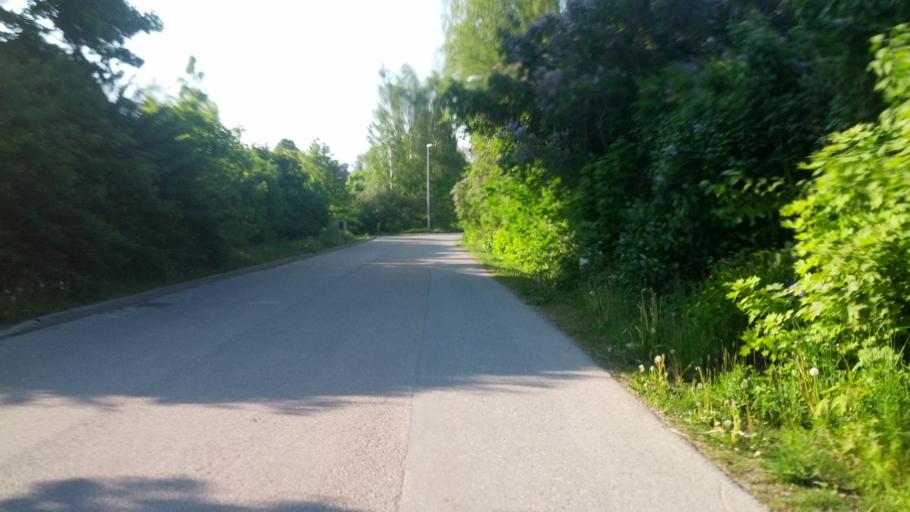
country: SE
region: Stockholm
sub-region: Vallentuna Kommun
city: Vallentuna
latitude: 59.5031
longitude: 18.0784
